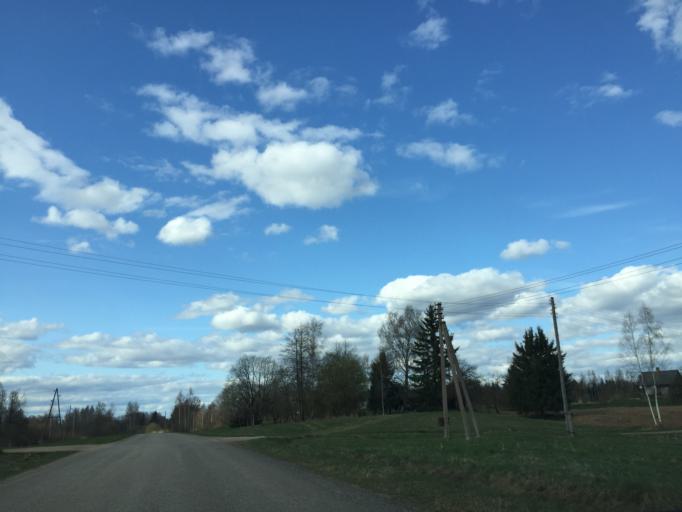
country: LV
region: Rezekne
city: Rezekne
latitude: 56.6128
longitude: 27.3176
